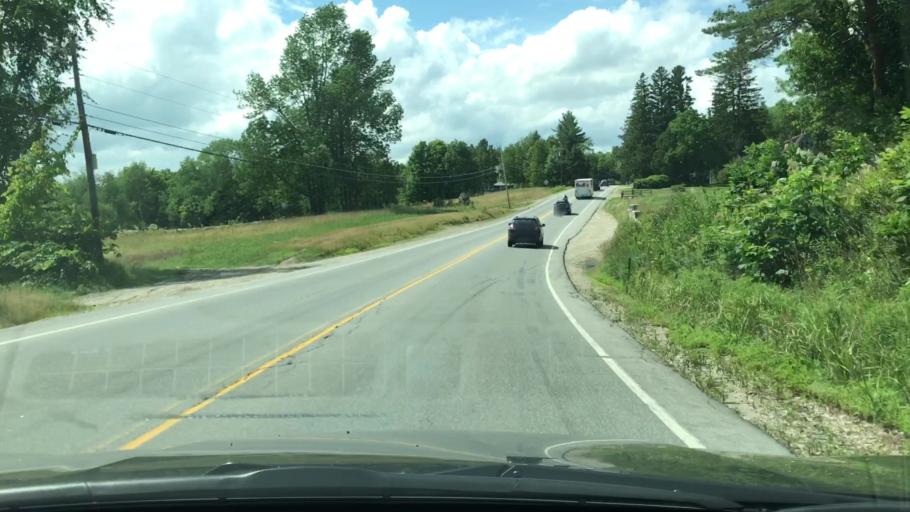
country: US
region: New Hampshire
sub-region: Coos County
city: Jefferson
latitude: 44.3682
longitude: -71.4017
